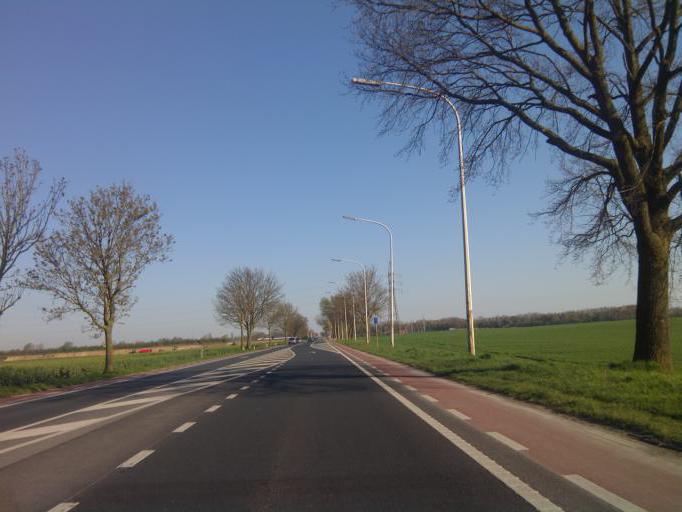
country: BE
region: Wallonia
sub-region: Province du Brabant Wallon
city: Louvain-la-Neuve
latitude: 50.6510
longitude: 4.6409
